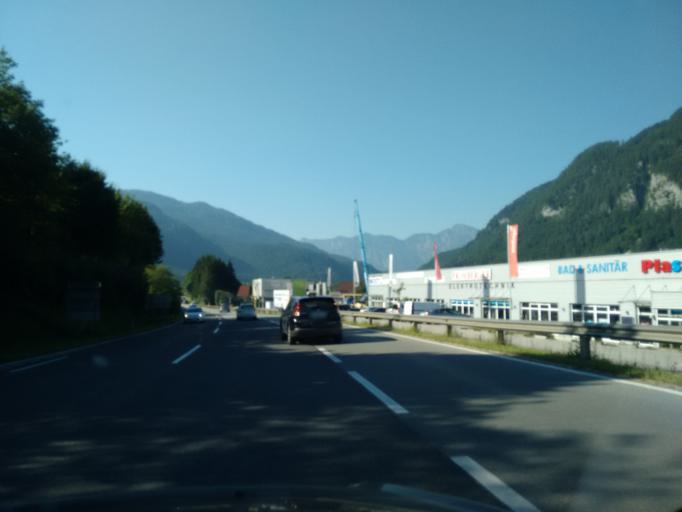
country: AT
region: Upper Austria
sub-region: Politischer Bezirk Gmunden
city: Bad Ischl
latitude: 47.6980
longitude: 13.6226
